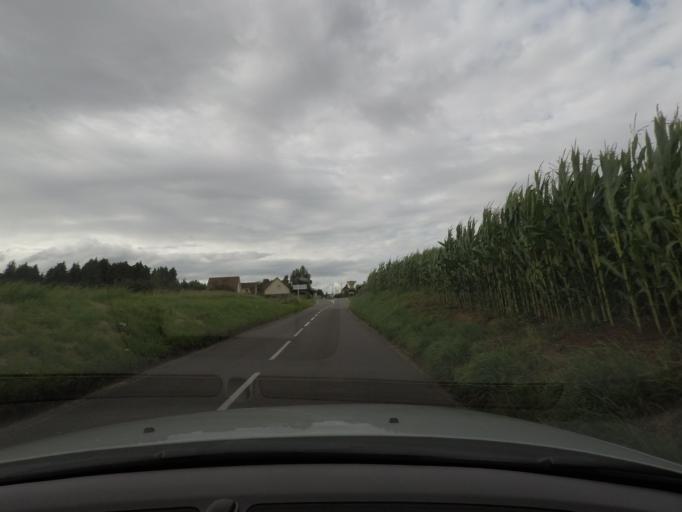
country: FR
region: Haute-Normandie
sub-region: Departement de la Seine-Maritime
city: Ymare
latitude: 49.3504
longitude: 1.1840
